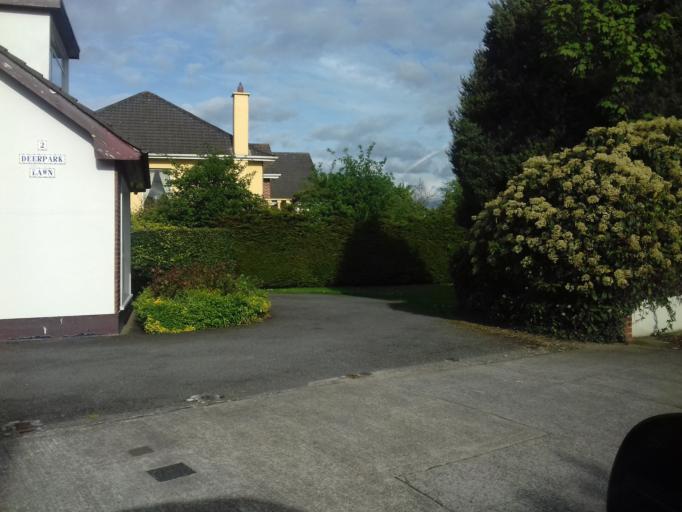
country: IE
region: Leinster
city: Castleknock
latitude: 53.3727
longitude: -6.3482
